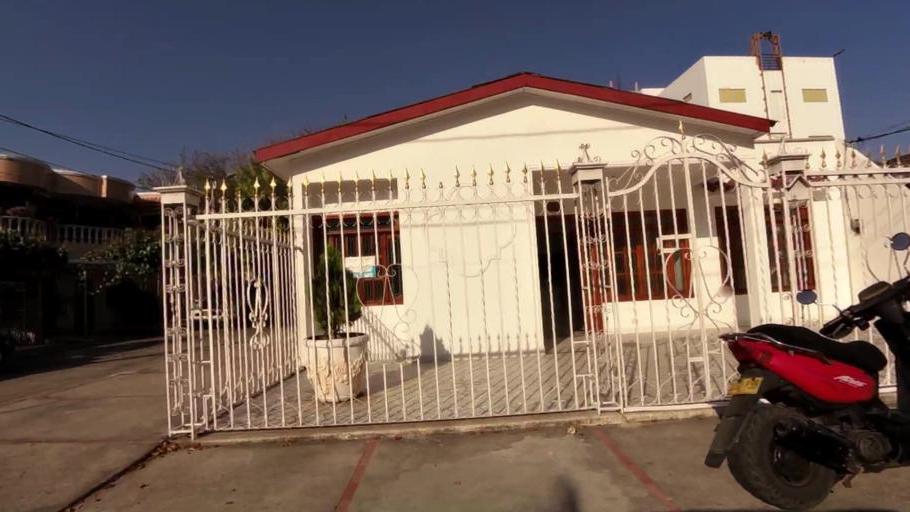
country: CO
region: Bolivar
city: Cartagena
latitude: 10.3974
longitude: -75.5211
